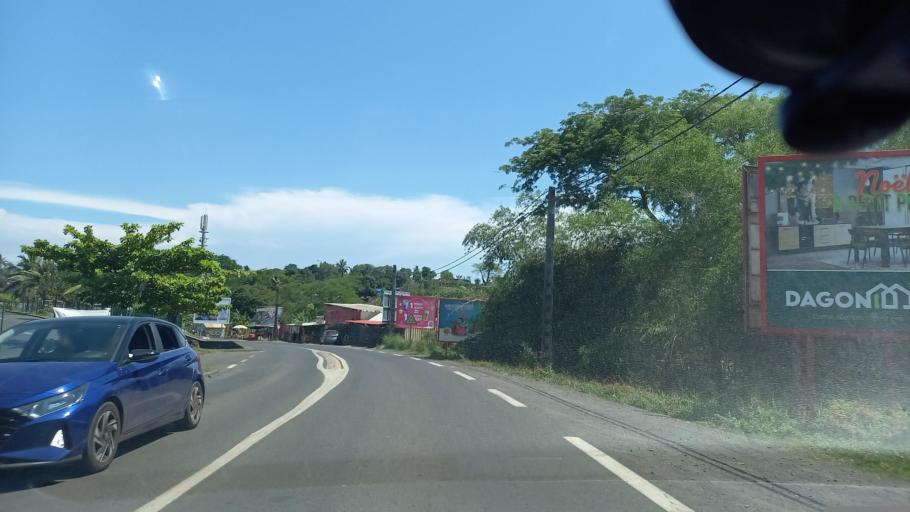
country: YT
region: Mamoudzou
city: Mamoudzou
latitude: -12.7576
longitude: 45.2327
